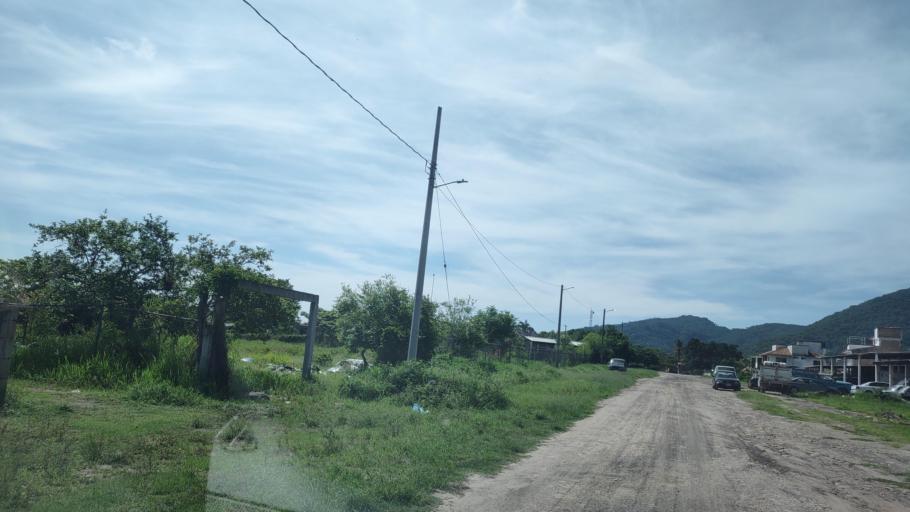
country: MX
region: Veracruz
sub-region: Emiliano Zapata
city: Dos Rios
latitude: 19.4286
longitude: -96.7987
